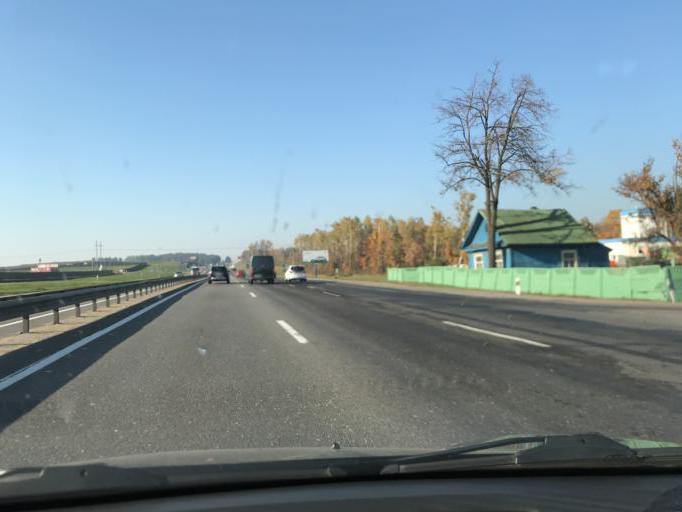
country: BY
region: Minsk
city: Pryvol'ny
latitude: 53.8092
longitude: 27.7844
